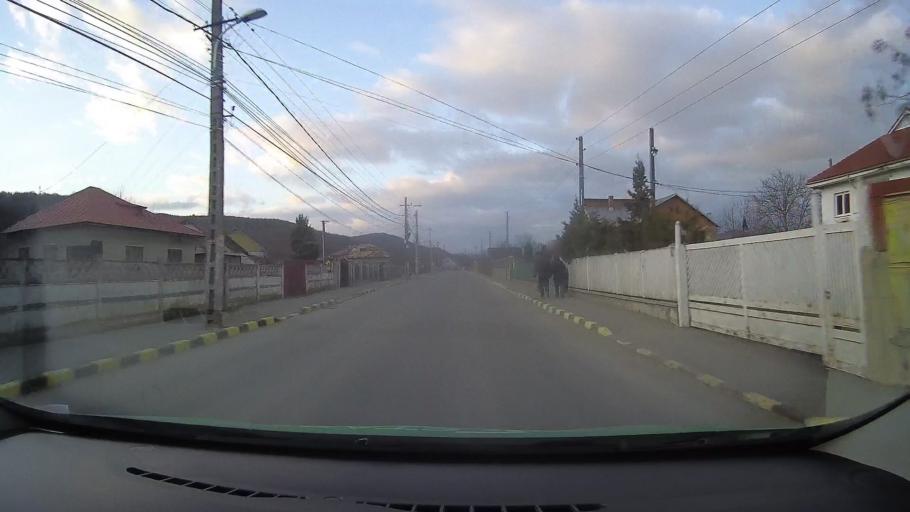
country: RO
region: Dambovita
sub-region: Municipiul Moreni
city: Moreni
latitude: 44.9876
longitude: 25.6383
